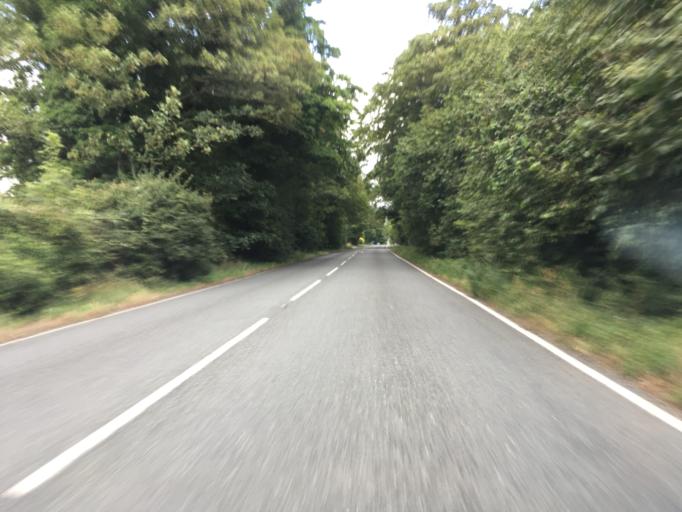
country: GB
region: England
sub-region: Hampshire
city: Kings Worthy
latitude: 51.1143
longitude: -1.2740
